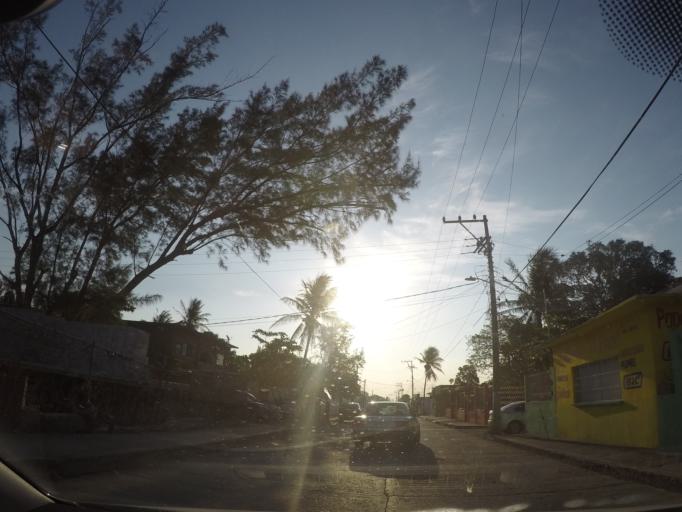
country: MX
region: Oaxaca
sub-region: Salina Cruz
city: Salina Cruz
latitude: 16.2031
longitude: -95.2004
